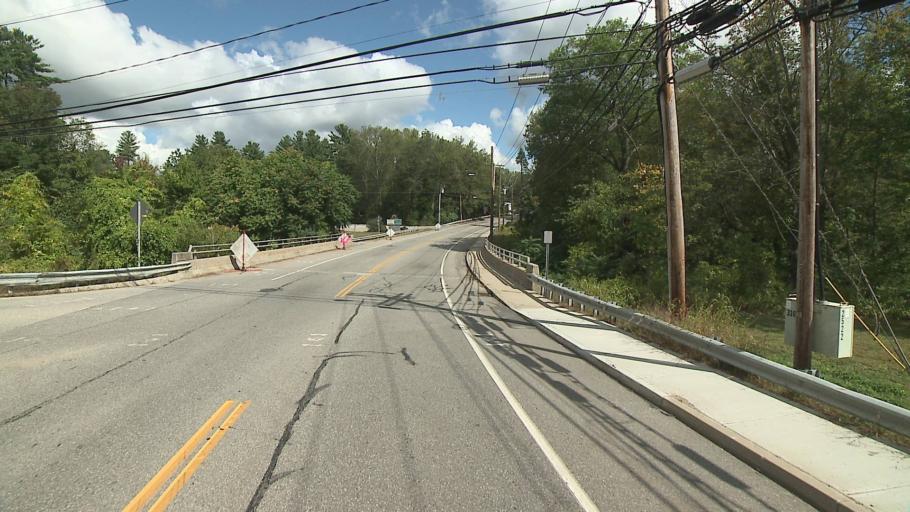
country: US
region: Connecticut
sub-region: Windham County
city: Putnam
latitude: 41.9117
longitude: -71.9160
